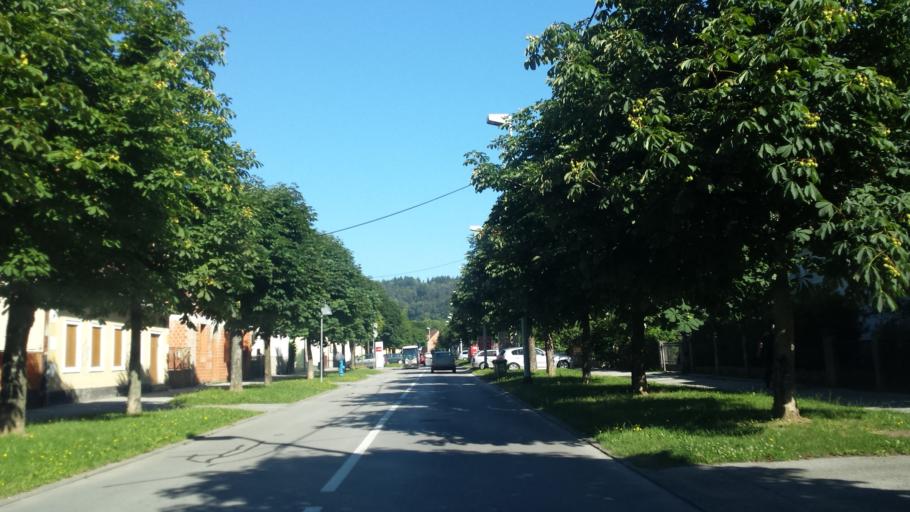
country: HR
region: Zagrebacka
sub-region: Grad Samobor
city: Samobor
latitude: 45.7999
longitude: 15.7190
